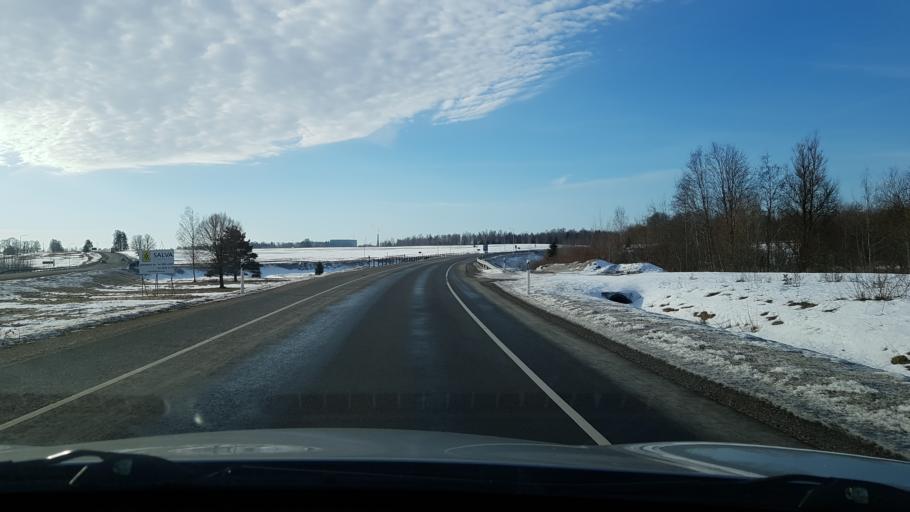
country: EE
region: Viljandimaa
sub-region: Viljandi linn
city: Viljandi
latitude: 58.4047
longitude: 25.5921
